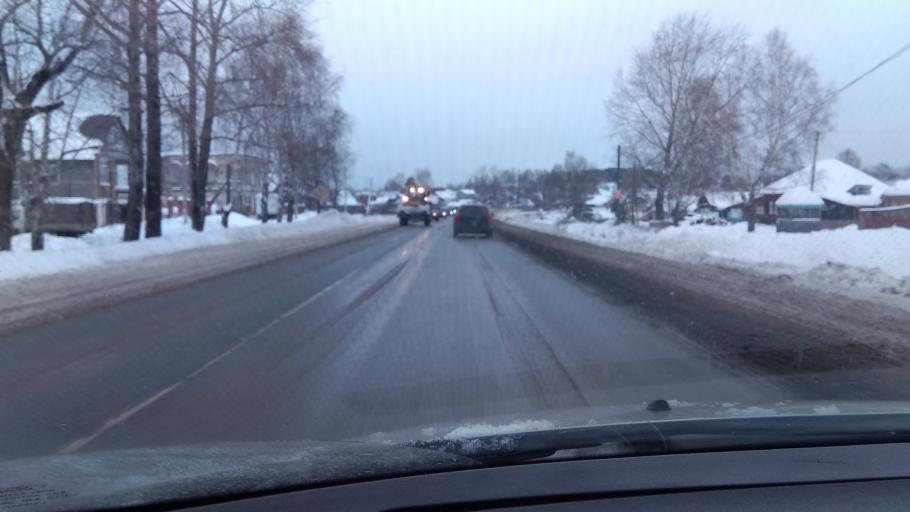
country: RU
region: Sverdlovsk
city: Nikolo-Pavlovskoye
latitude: 57.7839
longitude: 60.0584
